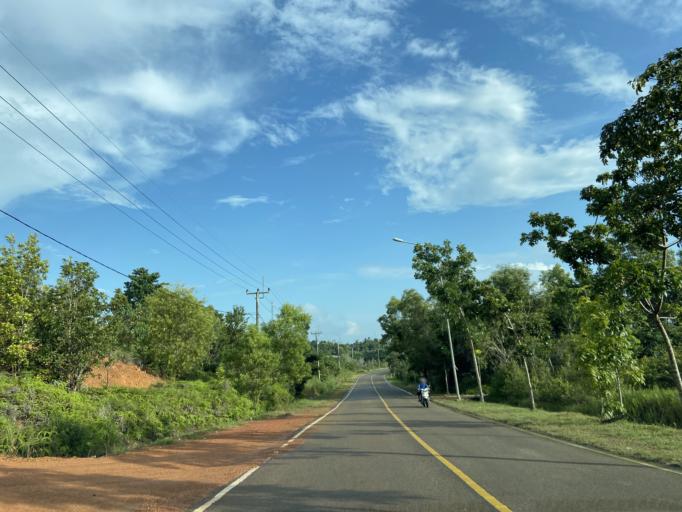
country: ID
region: Riau Islands
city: Tanjungpinang
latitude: 0.9454
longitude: 104.0581
